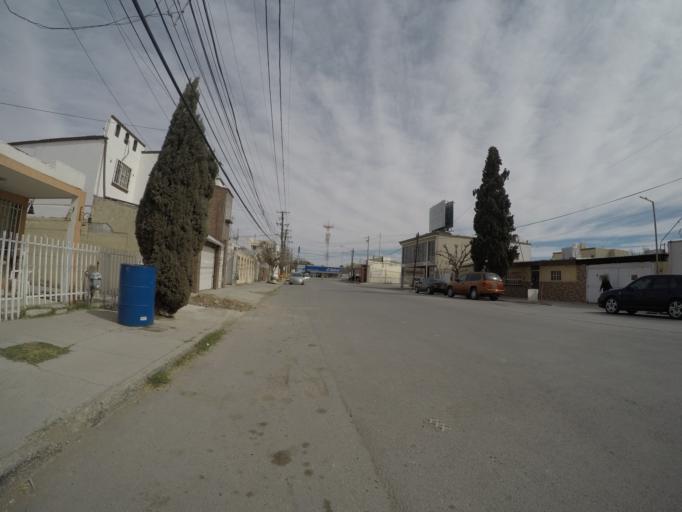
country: MX
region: Chihuahua
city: Ciudad Juarez
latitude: 31.7210
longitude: -106.4256
